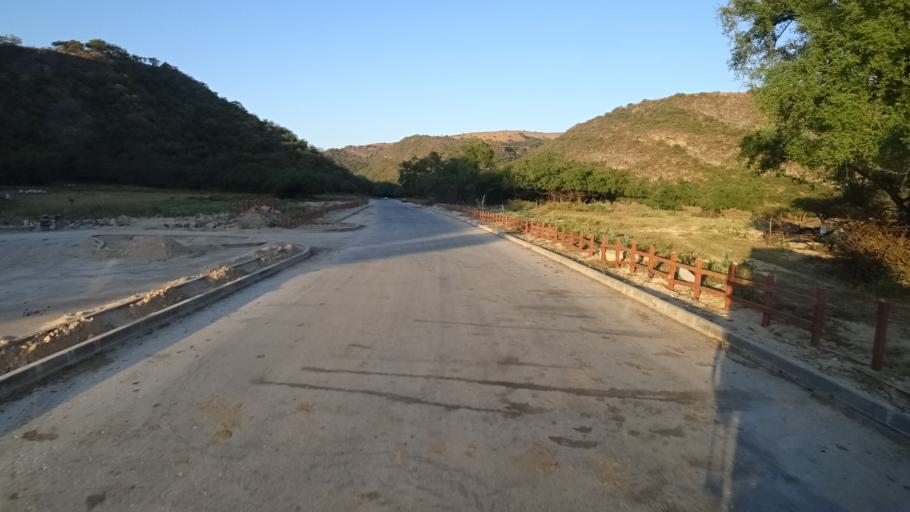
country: OM
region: Zufar
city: Salalah
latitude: 17.0916
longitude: 54.4460
